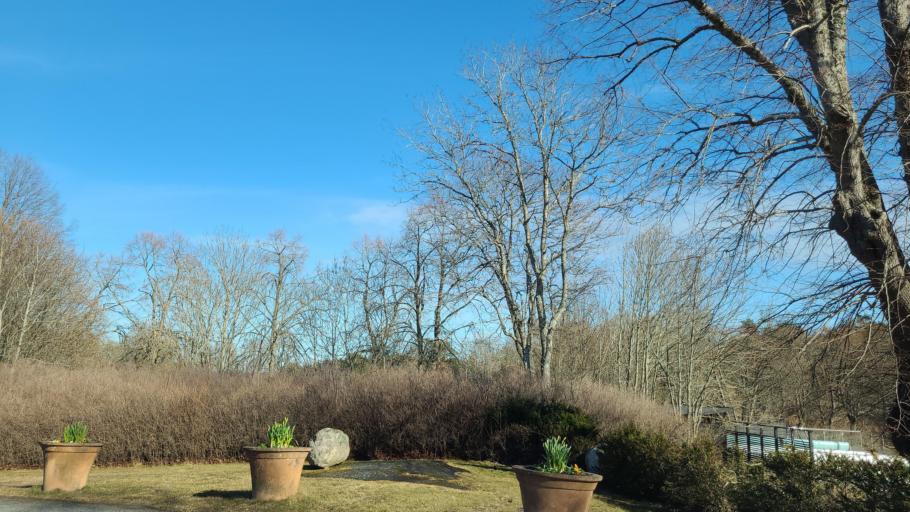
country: SE
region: Stockholm
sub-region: Varmdo Kommun
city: Hemmesta
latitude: 59.2760
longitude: 18.5613
